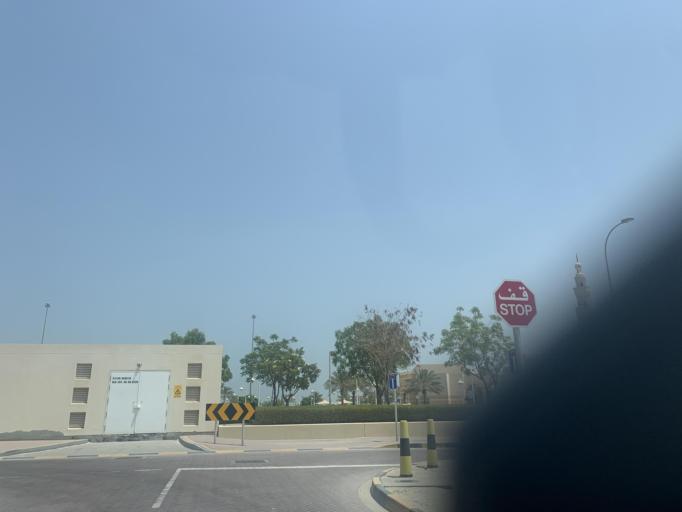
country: BH
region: Muharraq
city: Al Muharraq
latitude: 26.2967
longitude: 50.6411
